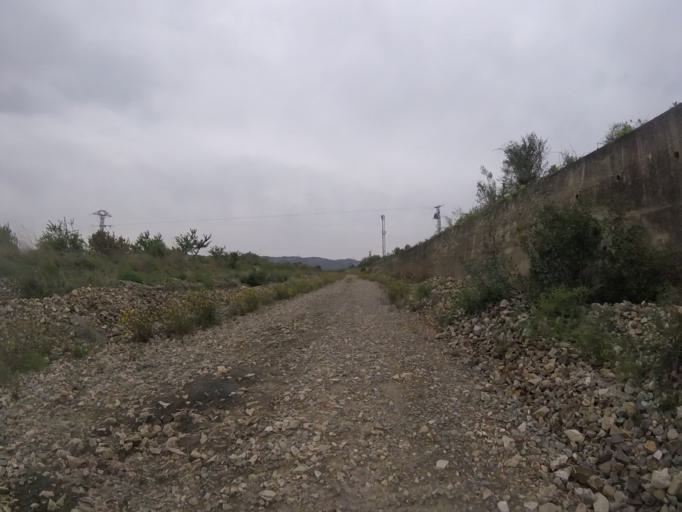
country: ES
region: Valencia
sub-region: Provincia de Castello
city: Alcoceber
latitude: 40.2633
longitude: 0.2578
